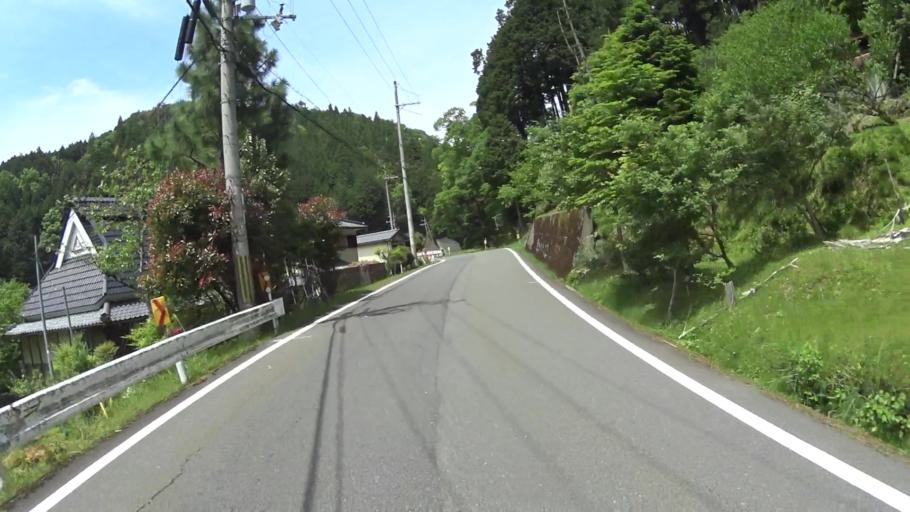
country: JP
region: Kyoto
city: Maizuru
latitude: 35.4131
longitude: 135.4620
